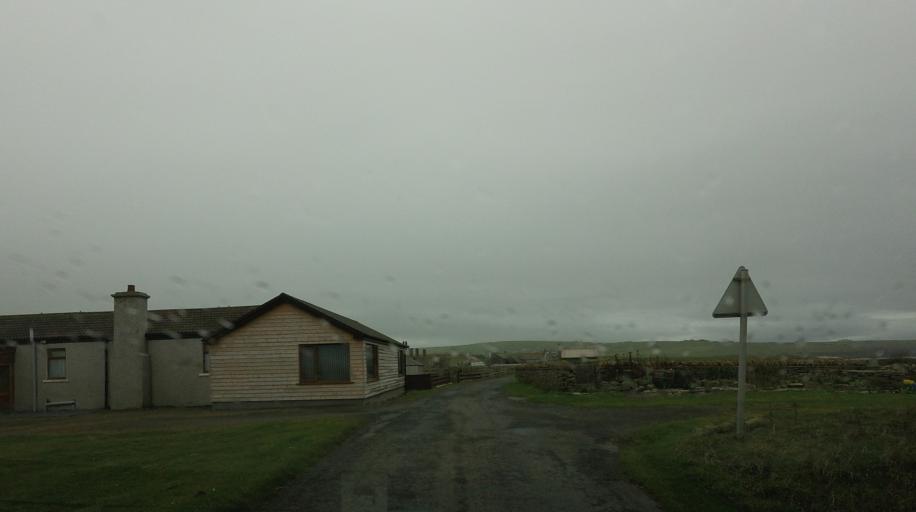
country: GB
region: Scotland
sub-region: Orkney Islands
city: Stromness
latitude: 59.1319
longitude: -3.3170
